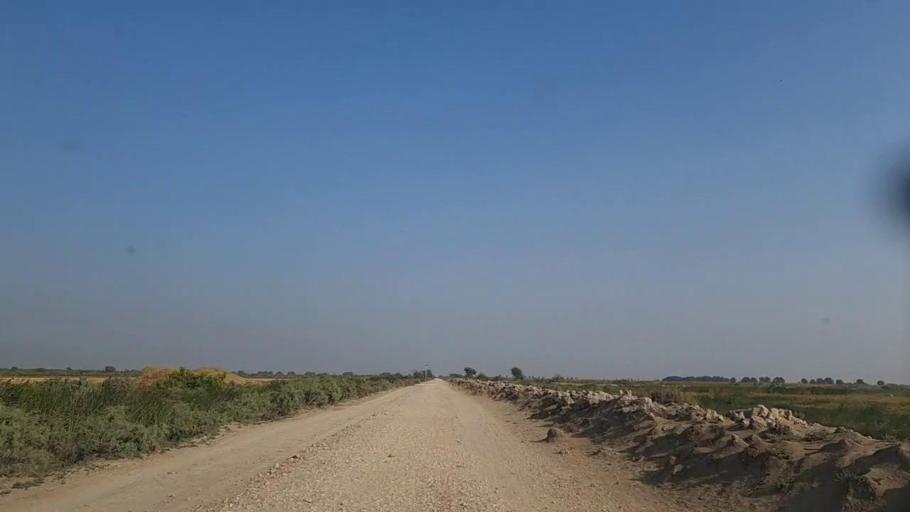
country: PK
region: Sindh
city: Jati
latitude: 24.4601
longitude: 68.2938
